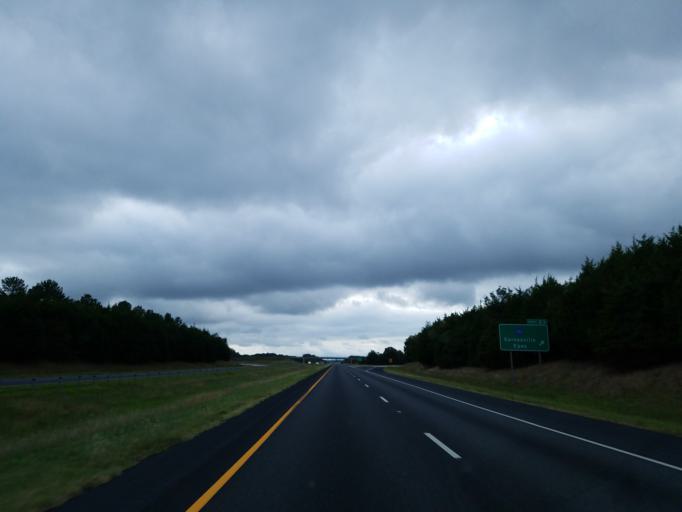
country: US
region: Alabama
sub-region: Sumter County
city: Livingston
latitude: 32.7060
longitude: -88.1375
